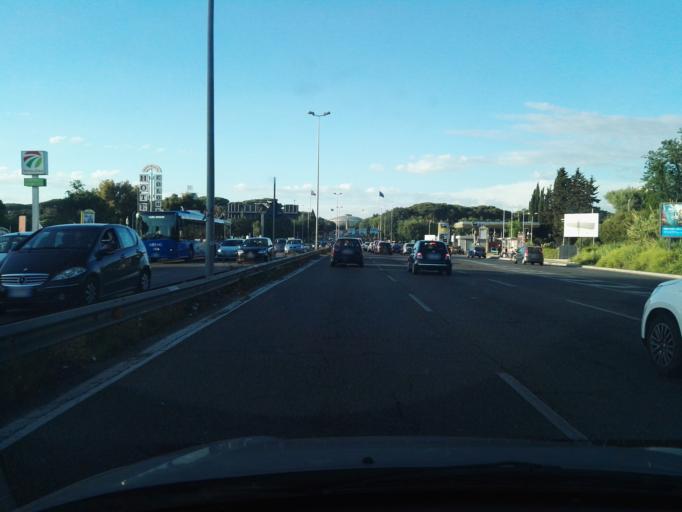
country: IT
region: Latium
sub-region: Citta metropolitana di Roma Capitale
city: Selcetta
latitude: 41.8163
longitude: 12.4619
